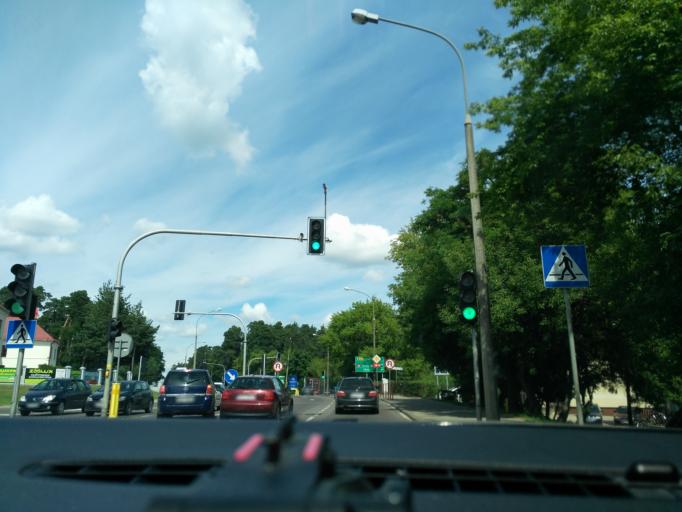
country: PL
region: Podlasie
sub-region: Powiat augustowski
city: Augustow
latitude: 53.8461
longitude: 22.9984
